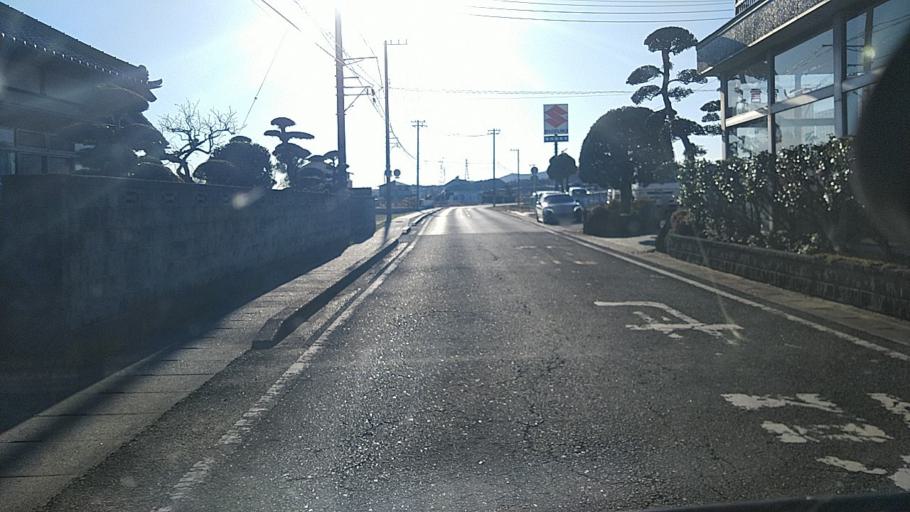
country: JP
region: Chiba
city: Kimitsu
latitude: 35.3154
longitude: 139.9083
